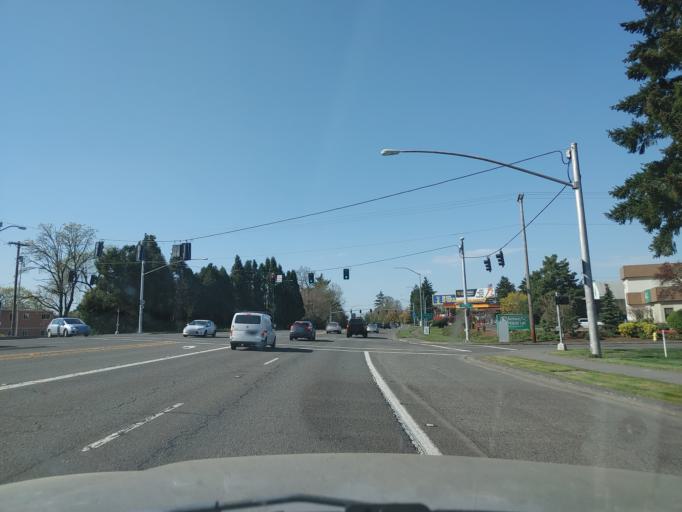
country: US
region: Oregon
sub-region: Clackamas County
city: Milwaukie
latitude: 45.4449
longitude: -122.6314
